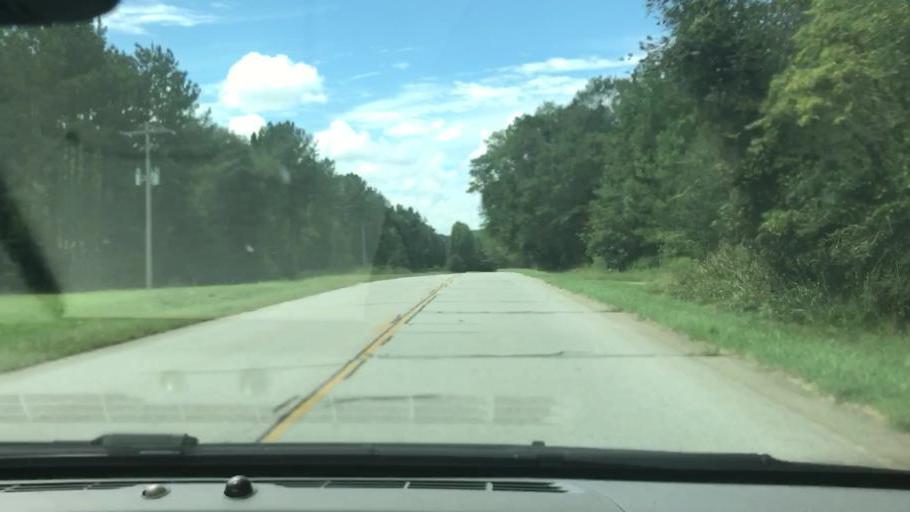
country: US
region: Georgia
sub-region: Stewart County
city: Lumpkin
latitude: 32.1423
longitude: -84.8403
